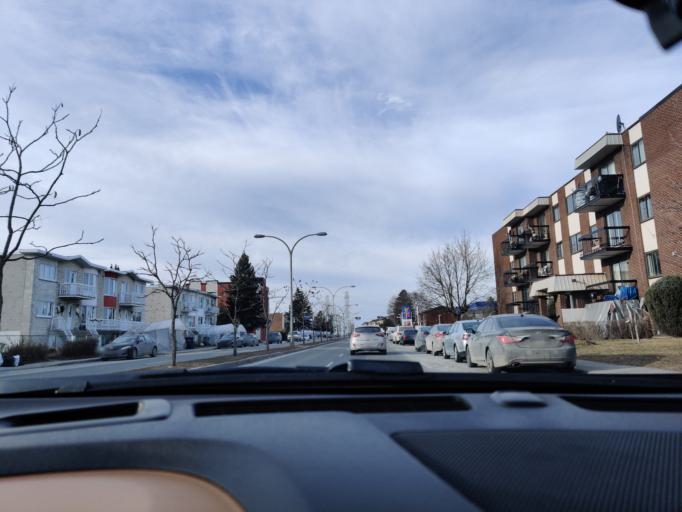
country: CA
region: Quebec
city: Dollard-Des Ormeaux
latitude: 45.5265
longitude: -73.7678
